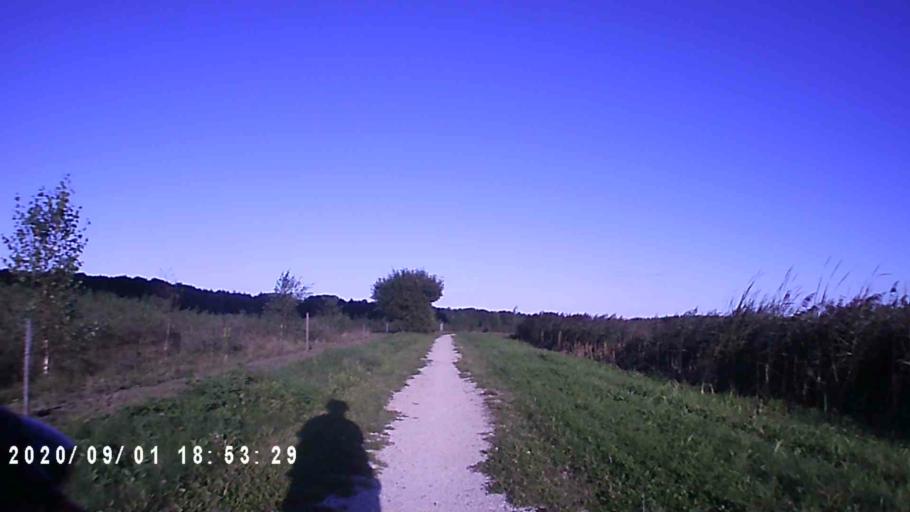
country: NL
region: Groningen
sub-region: Gemeente Veendam
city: Veendam
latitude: 53.1342
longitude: 6.8453
